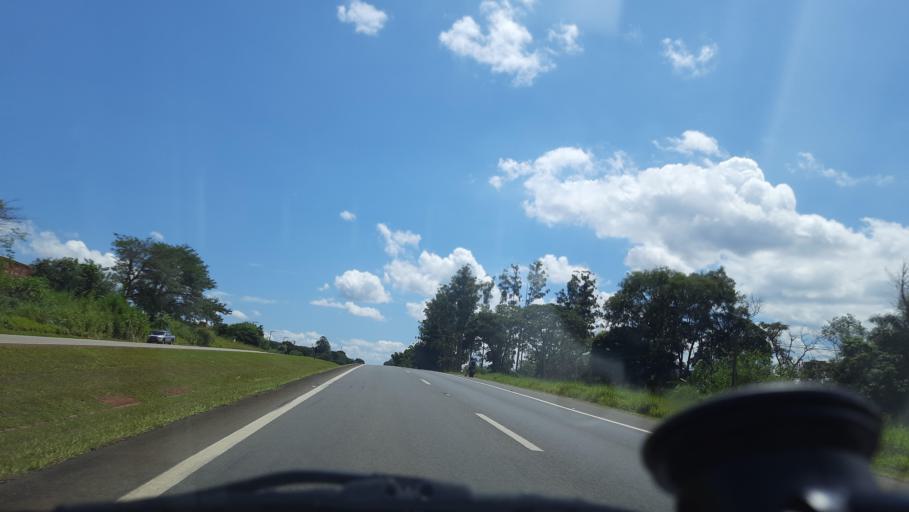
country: BR
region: Sao Paulo
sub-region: Moji-Guacu
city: Mogi-Gaucu
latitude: -22.2447
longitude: -46.9779
